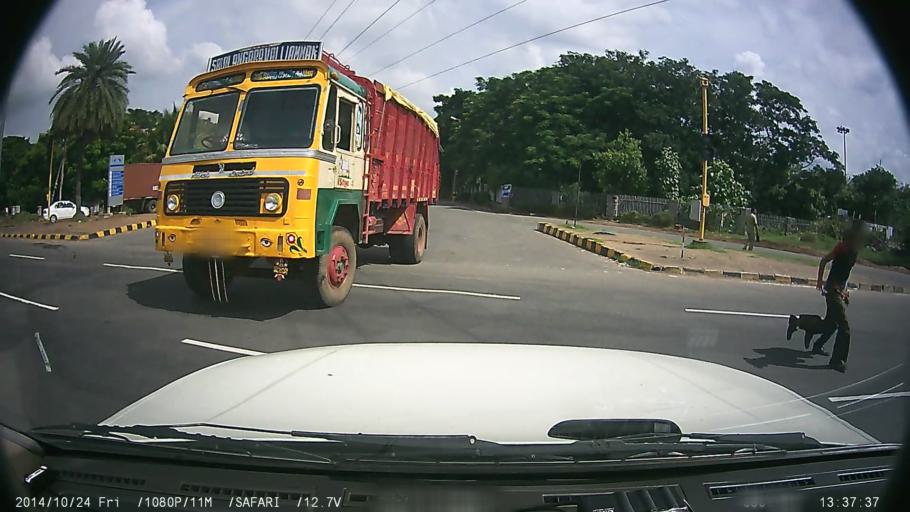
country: IN
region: Tamil Nadu
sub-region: Kancheepuram
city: Singapperumalkovil
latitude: 12.7863
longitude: 80.0147
